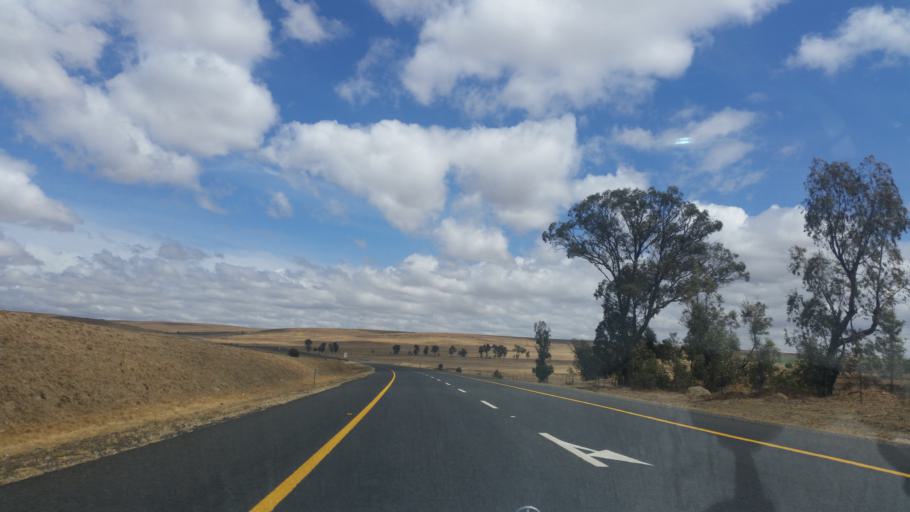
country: ZA
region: Orange Free State
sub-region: Thabo Mofutsanyana District Municipality
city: Harrismith
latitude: -28.2739
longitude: 28.9935
